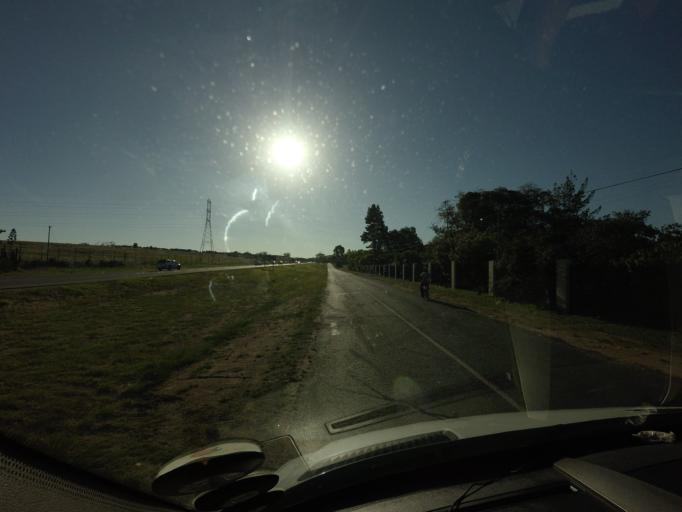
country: ZA
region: Western Cape
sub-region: Cape Winelands District Municipality
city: Stellenbosch
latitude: -33.9530
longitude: 18.7930
